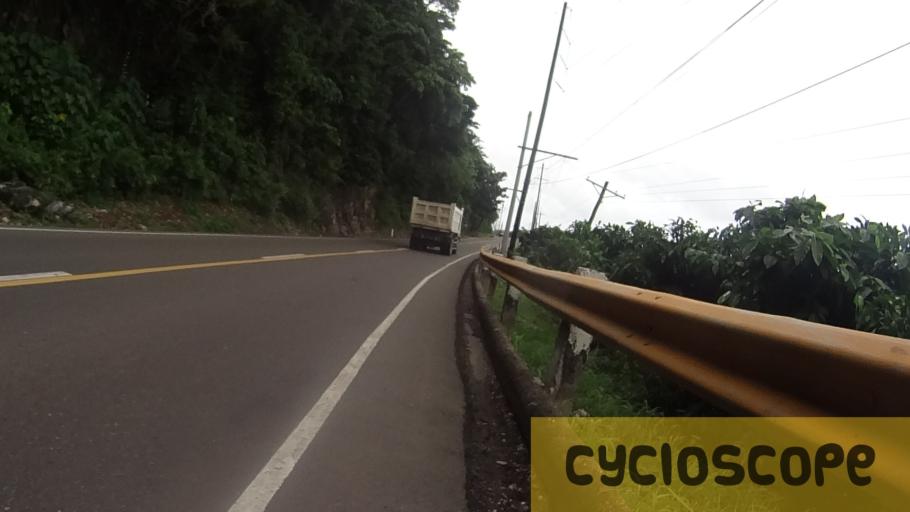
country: PH
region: Western Visayas
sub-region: Province of Aklan
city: Gibong
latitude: 11.8668
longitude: 122.0356
